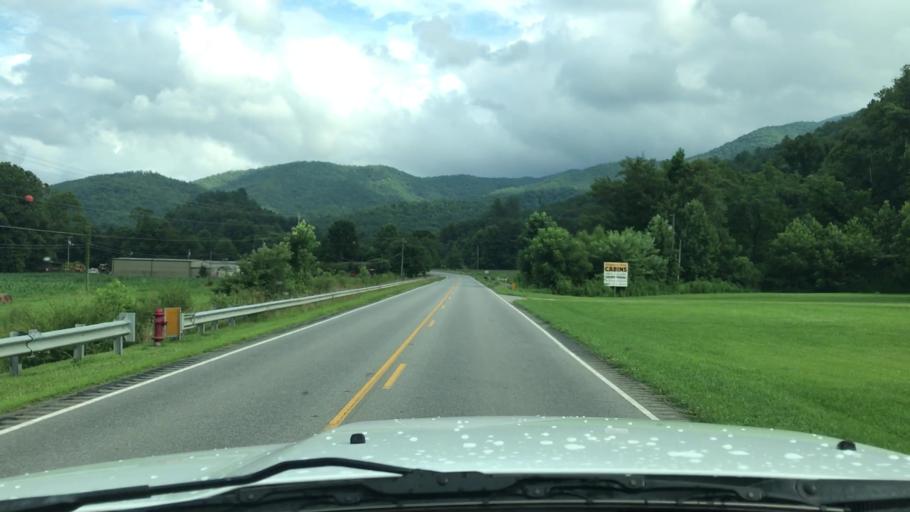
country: US
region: North Carolina
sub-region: Graham County
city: Robbinsville
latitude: 35.3005
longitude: -83.7952
